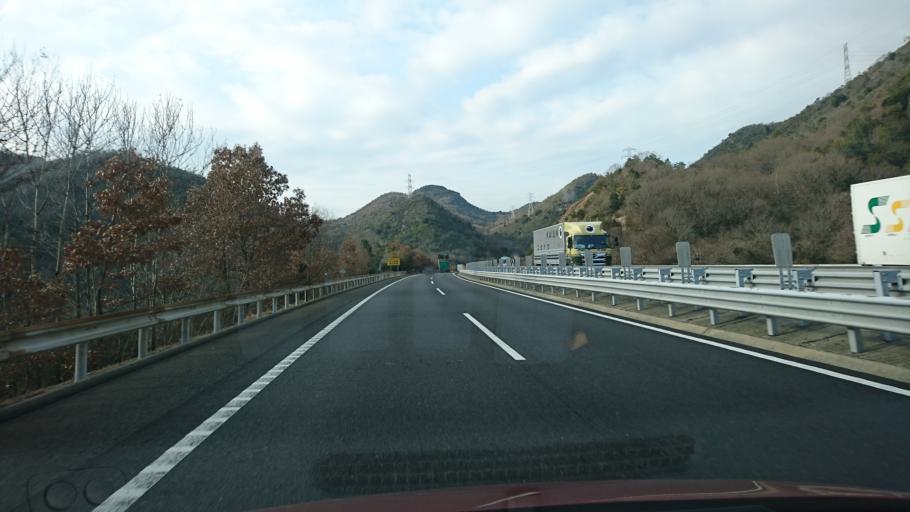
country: JP
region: Hyogo
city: Aioi
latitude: 34.7961
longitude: 134.4329
